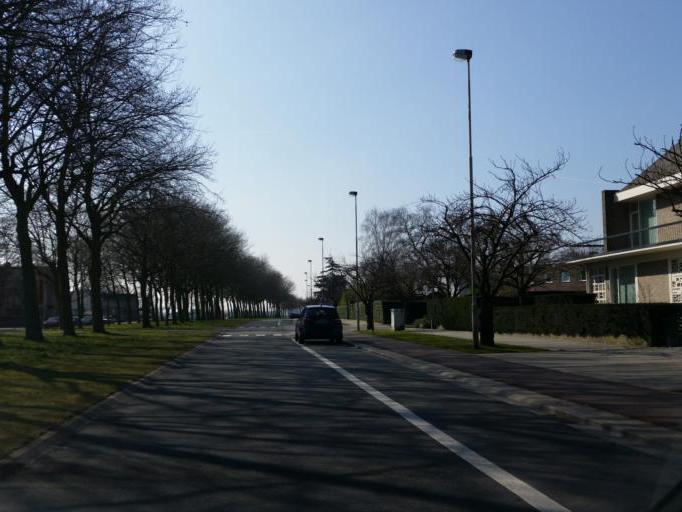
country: BE
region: Flanders
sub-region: Provincie Antwerpen
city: Antwerpen
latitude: 51.2171
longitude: 4.3846
